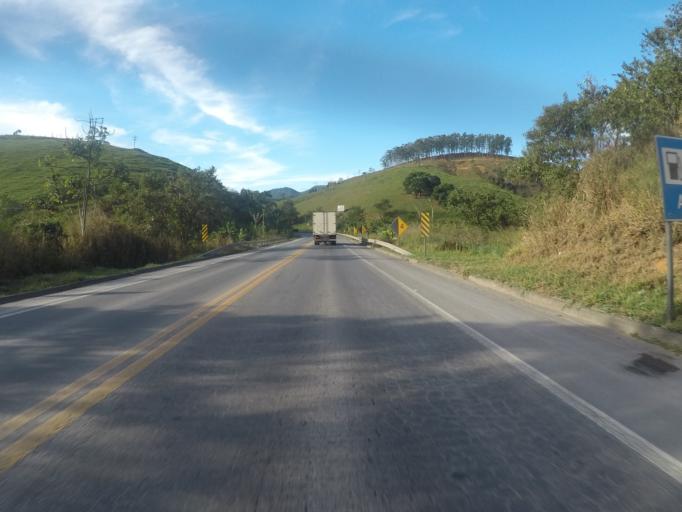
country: BR
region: Espirito Santo
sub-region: Ibiracu
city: Ibiracu
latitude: -19.8378
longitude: -40.3816
